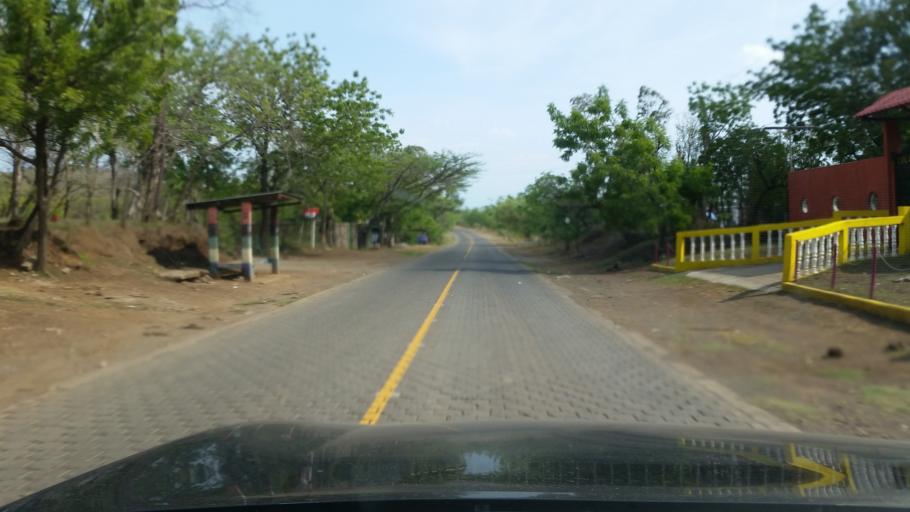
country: NI
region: Managua
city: Carlos Fonseca Amador
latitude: 12.0191
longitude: -86.5169
